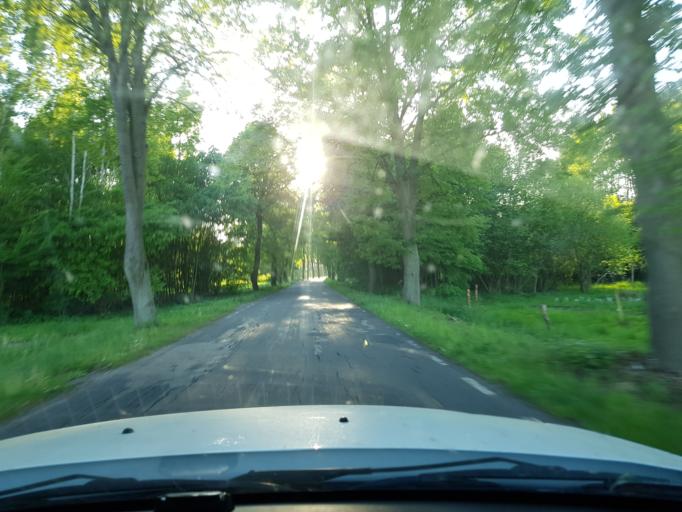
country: PL
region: West Pomeranian Voivodeship
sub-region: Powiat goleniowski
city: Maszewo
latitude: 53.4810
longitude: 14.9959
